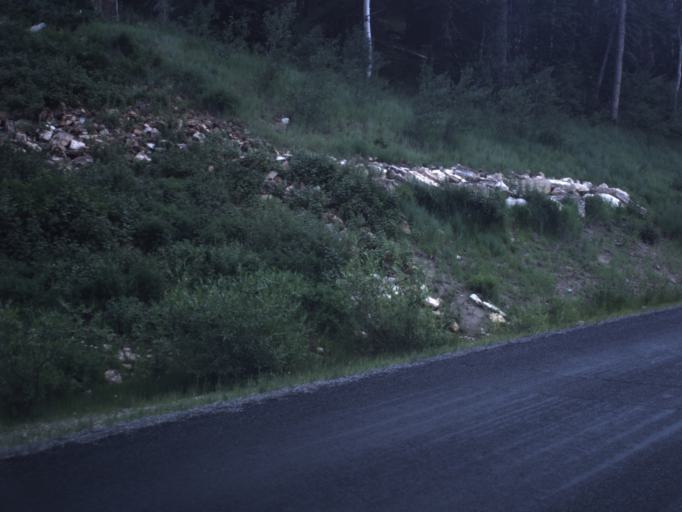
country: US
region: Utah
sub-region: Summit County
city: Francis
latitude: 40.4921
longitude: -111.0342
